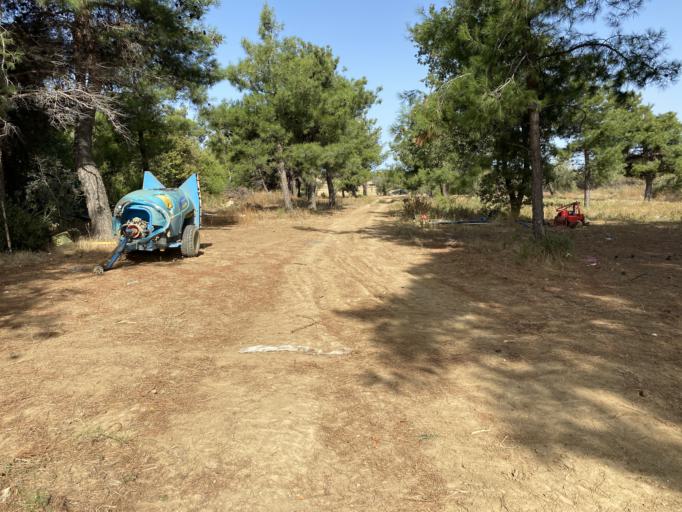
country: TR
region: Canakkale
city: Eceabat
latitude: 40.1808
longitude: 26.2875
